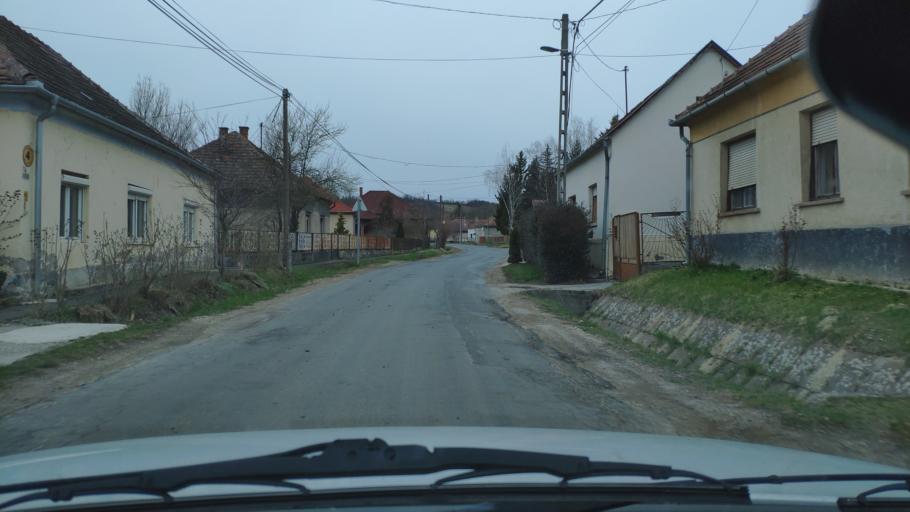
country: HU
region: Zala
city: Pacsa
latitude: 46.6748
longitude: 17.0554
